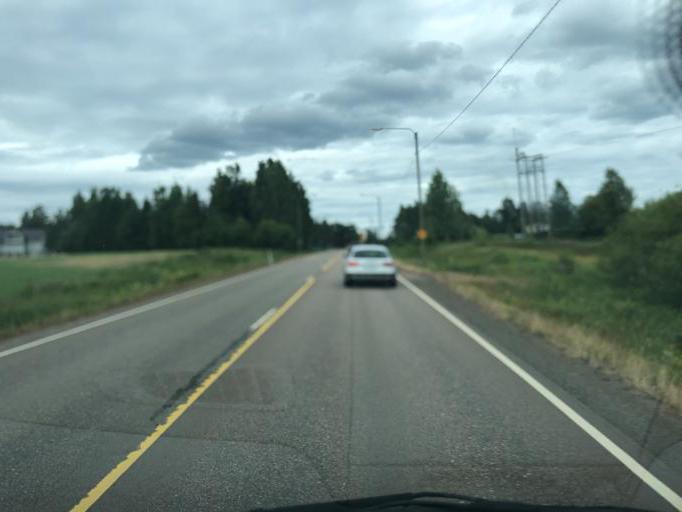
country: FI
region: Southern Savonia
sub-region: Mikkeli
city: Maentyharju
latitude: 61.0868
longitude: 27.0656
